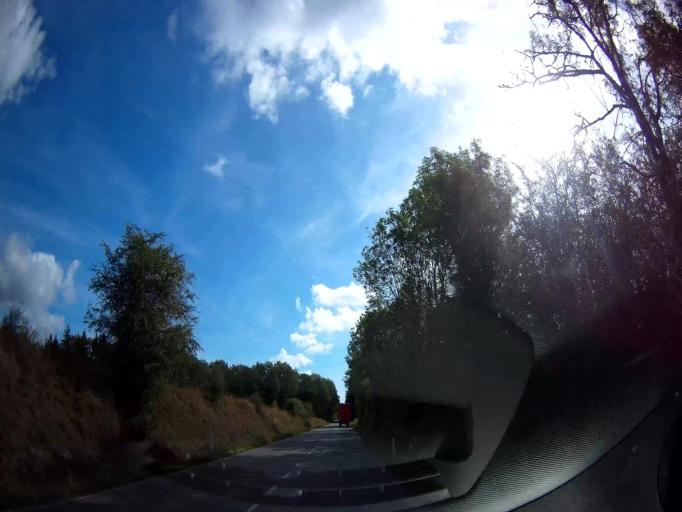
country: BE
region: Wallonia
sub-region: Province de Namur
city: Rochefort
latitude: 50.1670
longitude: 5.1388
